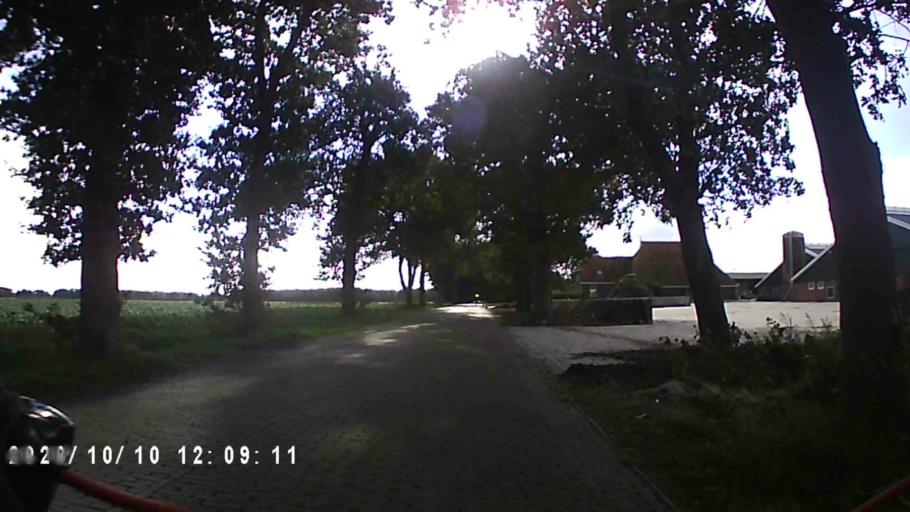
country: NL
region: Friesland
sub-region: Gemeente Heerenveen
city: Jubbega
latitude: 53.0468
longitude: 6.1437
